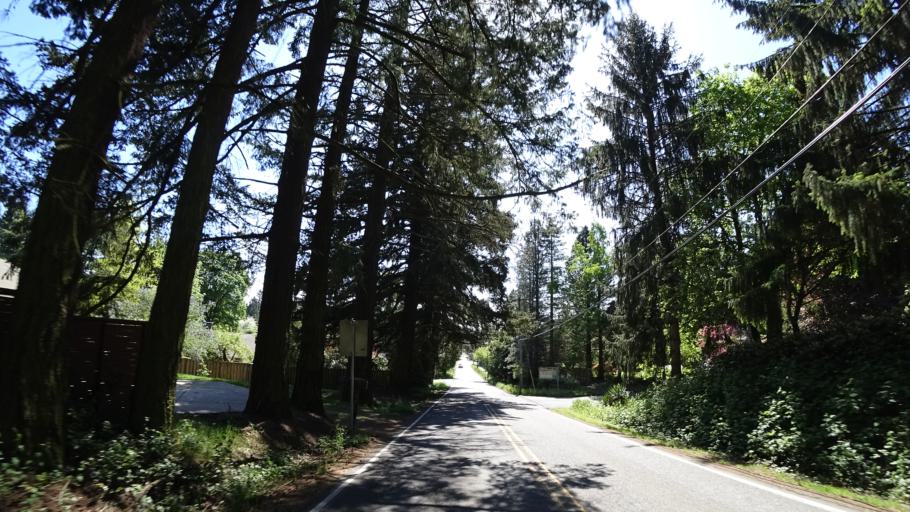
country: US
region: Oregon
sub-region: Washington County
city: Raleigh Hills
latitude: 45.4840
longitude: -122.7350
